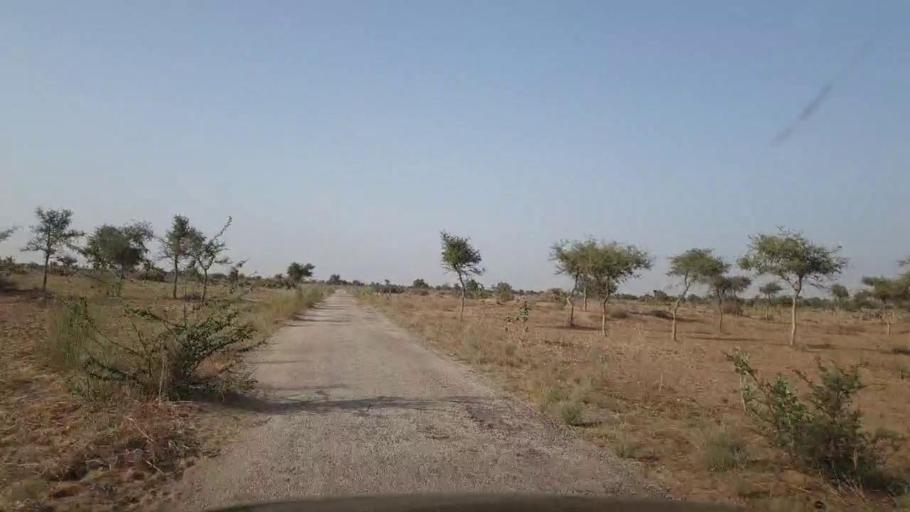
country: PK
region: Sindh
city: Islamkot
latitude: 25.1079
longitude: 70.4157
